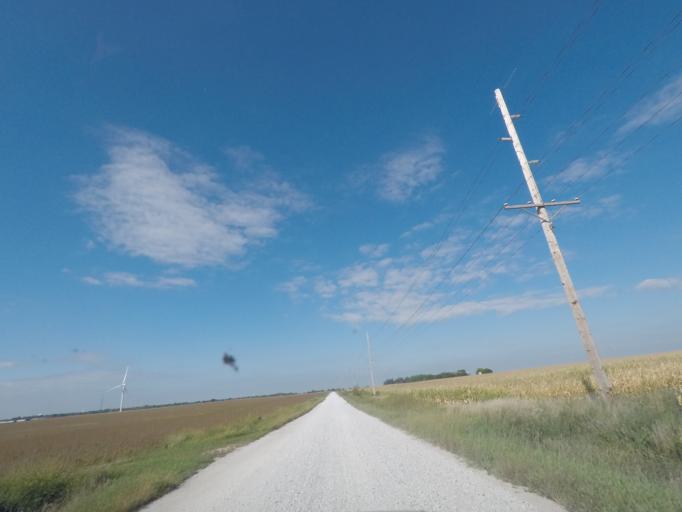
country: US
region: Iowa
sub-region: Story County
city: Nevada
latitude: 42.0344
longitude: -93.4153
